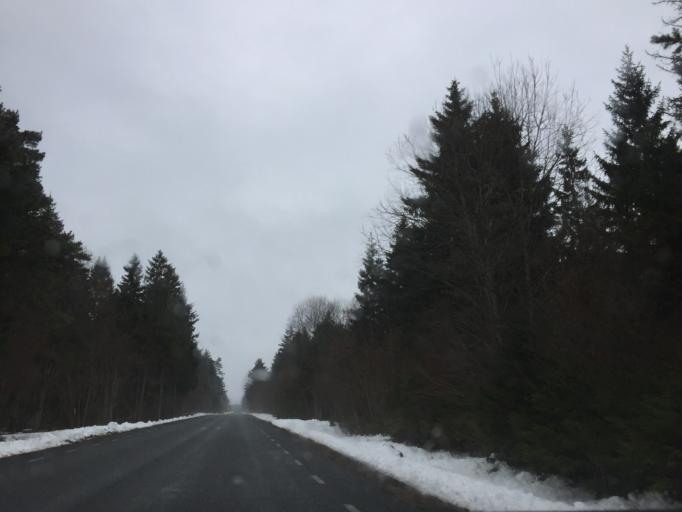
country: EE
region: Saare
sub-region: Kuressaare linn
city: Kuressaare
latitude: 58.3377
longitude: 22.0281
